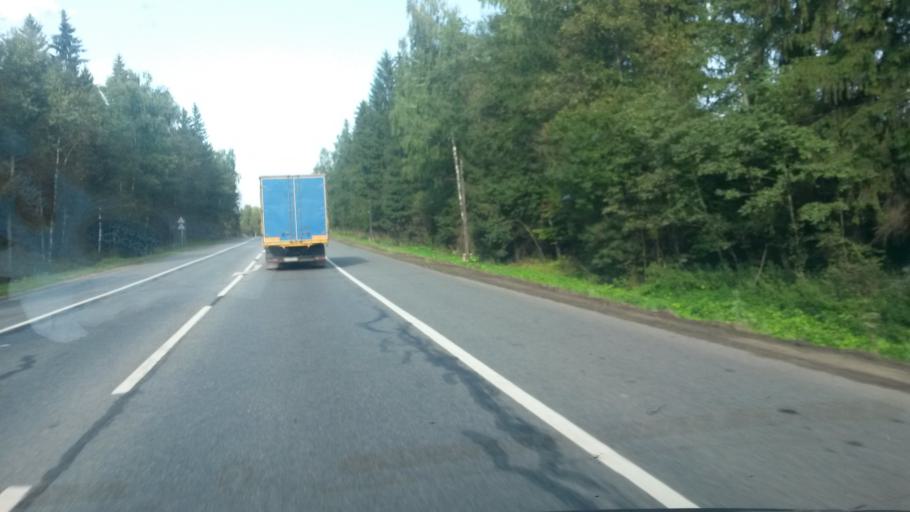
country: RU
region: Jaroslavl
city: Pereslavl'-Zalesskiy
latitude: 56.6450
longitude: 38.6890
